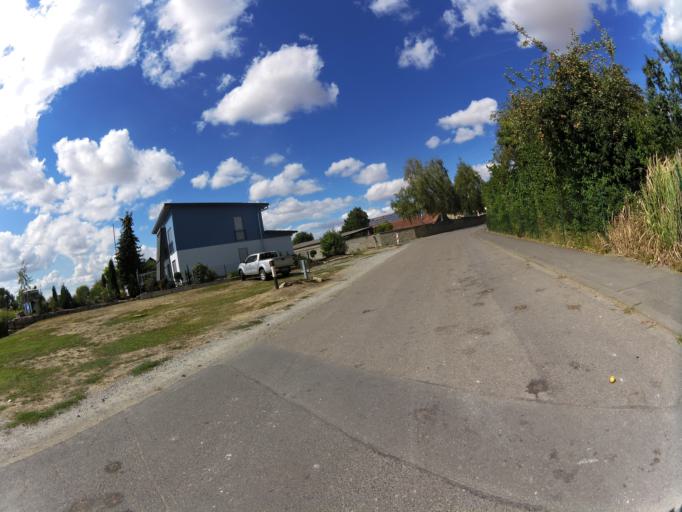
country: DE
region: Bavaria
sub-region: Regierungsbezirk Unterfranken
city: Sonderhofen
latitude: 49.5707
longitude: 10.0191
